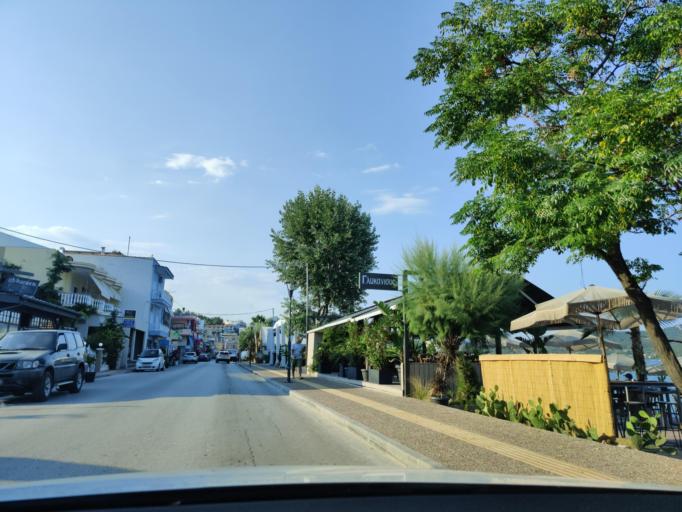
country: GR
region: East Macedonia and Thrace
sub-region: Nomos Kavalas
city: Nea Peramos
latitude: 40.8379
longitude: 24.3051
